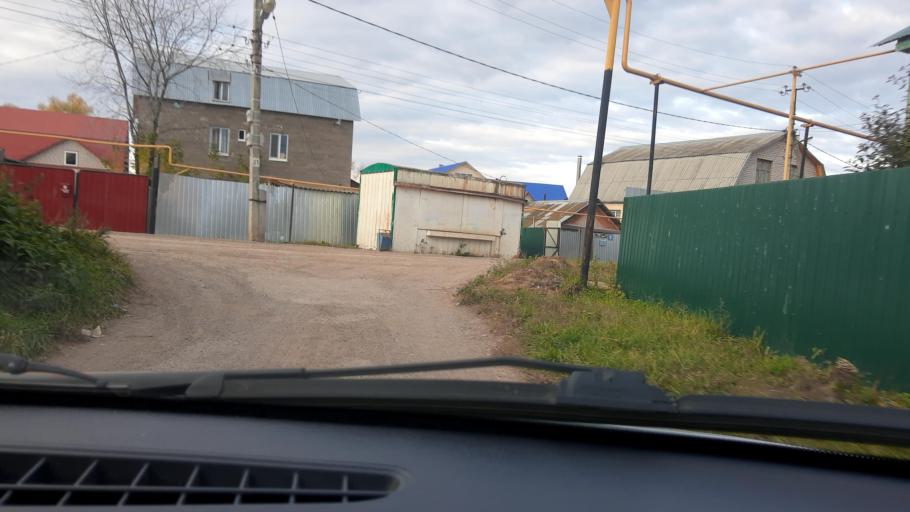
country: RU
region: Bashkortostan
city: Ufa
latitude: 54.7394
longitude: 55.9242
